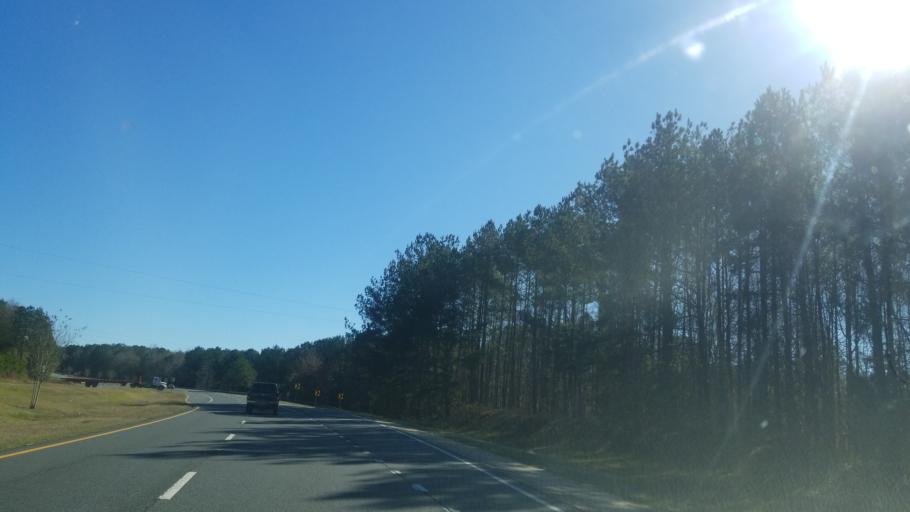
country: US
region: Georgia
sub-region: Talbot County
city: Talbotton
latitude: 32.5470
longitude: -84.7281
